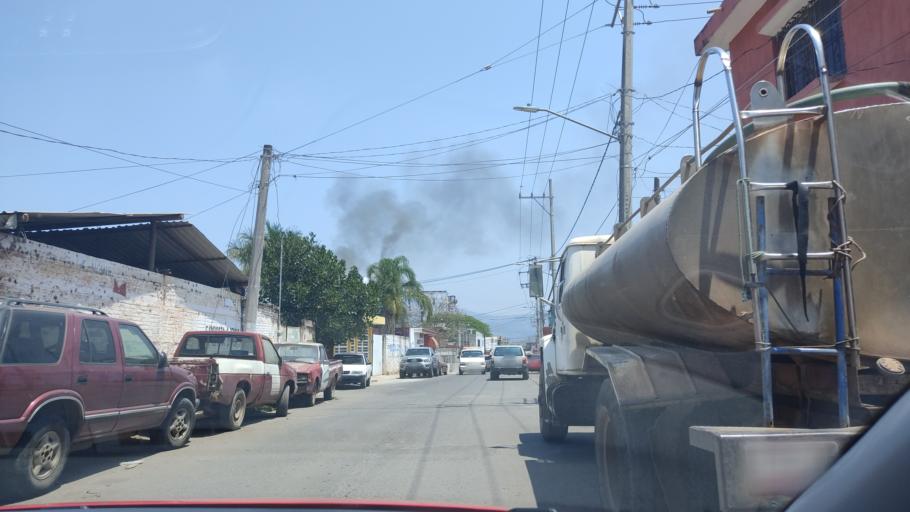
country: MX
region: Nayarit
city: Puga
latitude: 21.5814
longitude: -104.8246
